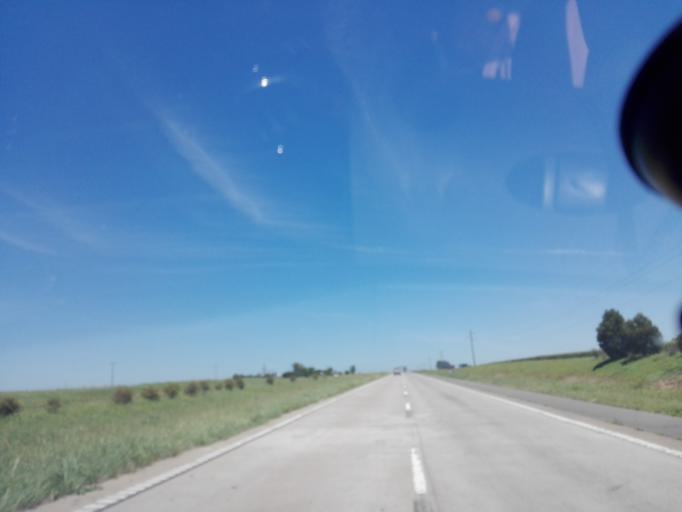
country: AR
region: Santa Fe
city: Canada de Gomez
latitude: -32.8503
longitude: -61.3684
